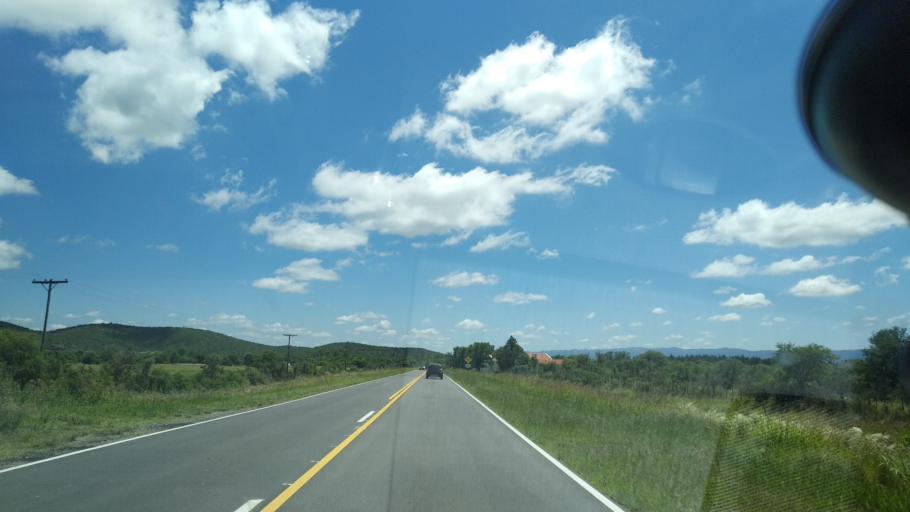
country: AR
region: Cordoba
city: Salsacate
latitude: -31.3590
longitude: -65.1032
